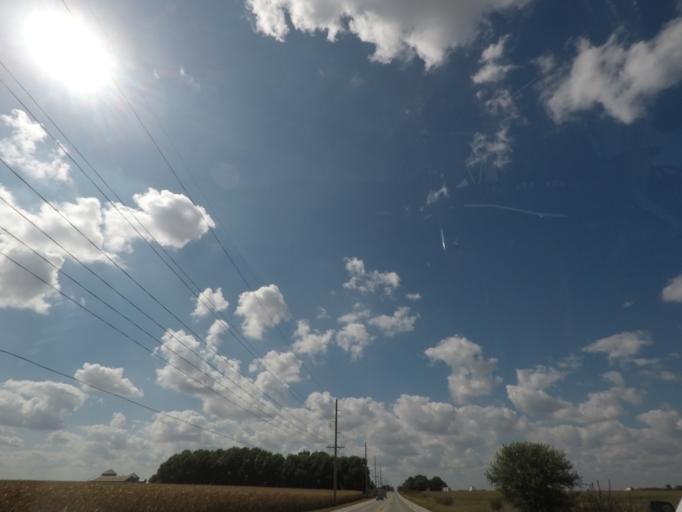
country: US
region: Iowa
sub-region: Story County
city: Nevada
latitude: 42.0231
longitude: -93.5272
